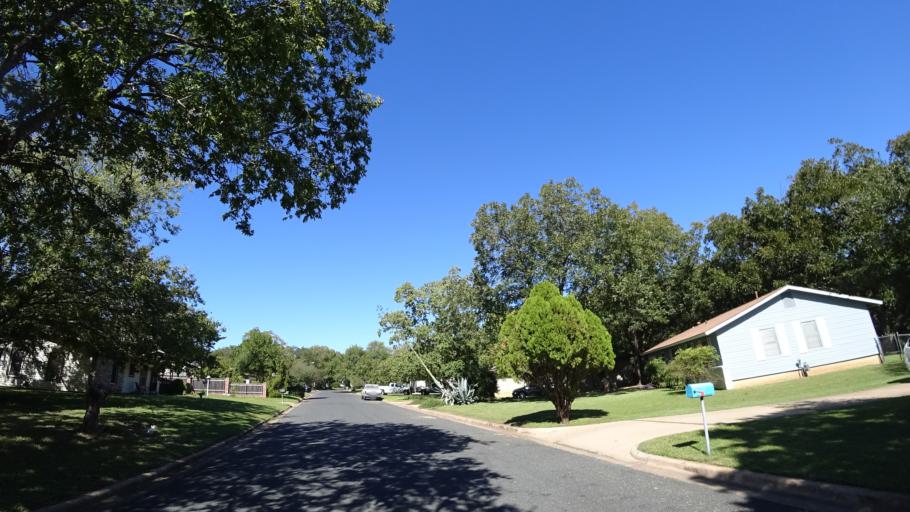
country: US
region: Texas
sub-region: Travis County
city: Rollingwood
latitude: 30.2204
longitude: -97.7850
